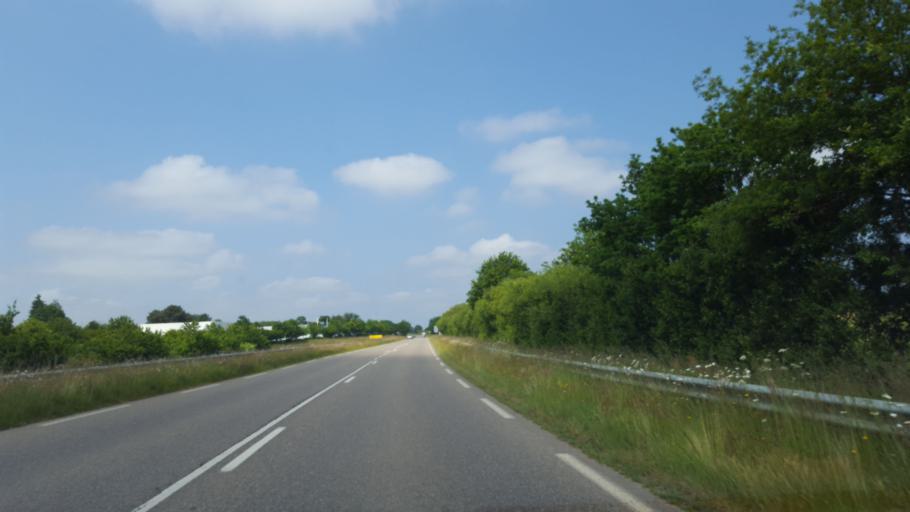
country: FR
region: Brittany
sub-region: Departement d'Ille-et-Vilaine
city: Maure-de-Bretagne
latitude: 47.9100
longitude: -1.9820
